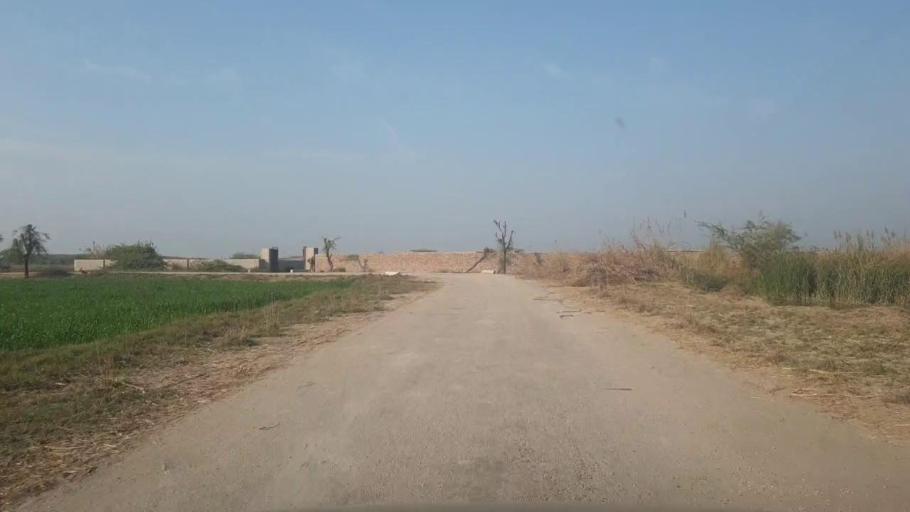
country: PK
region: Sindh
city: Sakrand
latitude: 26.0522
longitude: 68.3663
